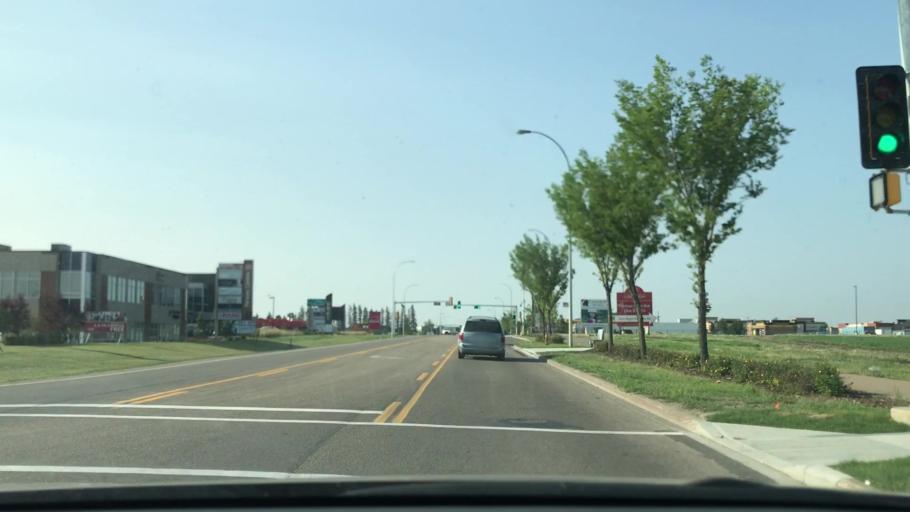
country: CA
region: Alberta
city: Beaumont
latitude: 53.4293
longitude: -113.4800
